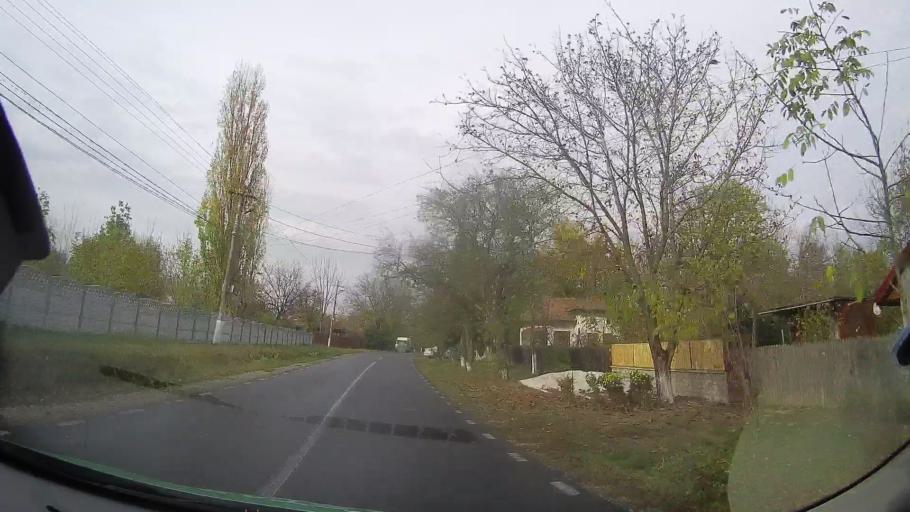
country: RO
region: Ialomita
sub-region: Comuna Fierbinti-Targ
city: Fierbinti-Targ
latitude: 44.7007
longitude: 26.3285
